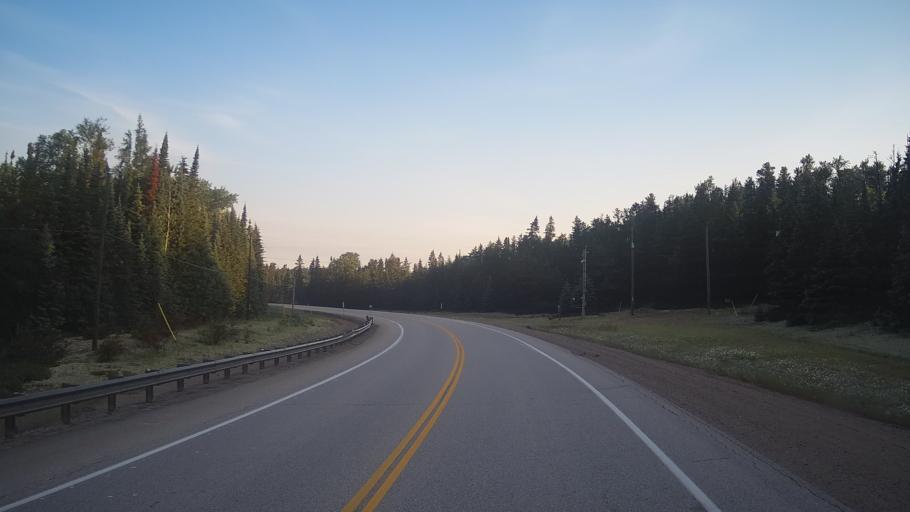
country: CA
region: Ontario
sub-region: Rainy River District
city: Atikokan
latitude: 49.2310
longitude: -90.9660
